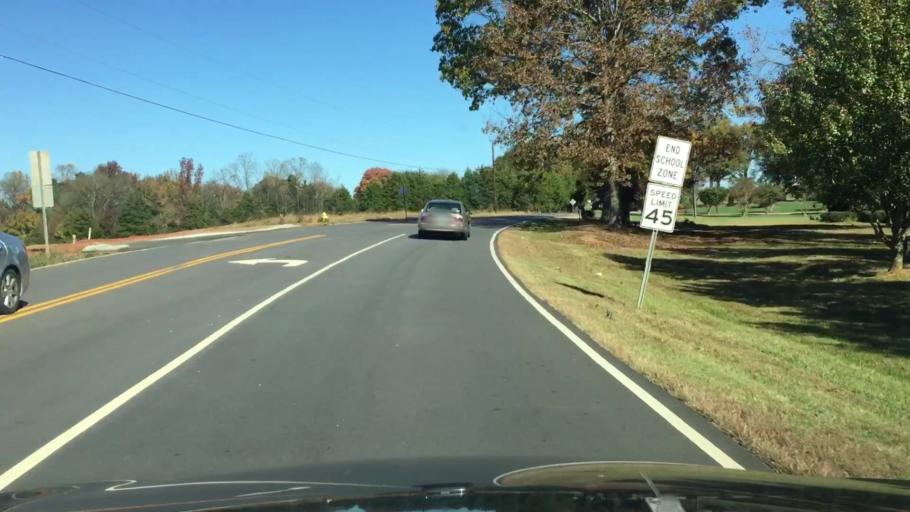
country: US
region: North Carolina
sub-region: Iredell County
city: Mooresville
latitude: 35.5460
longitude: -80.7756
